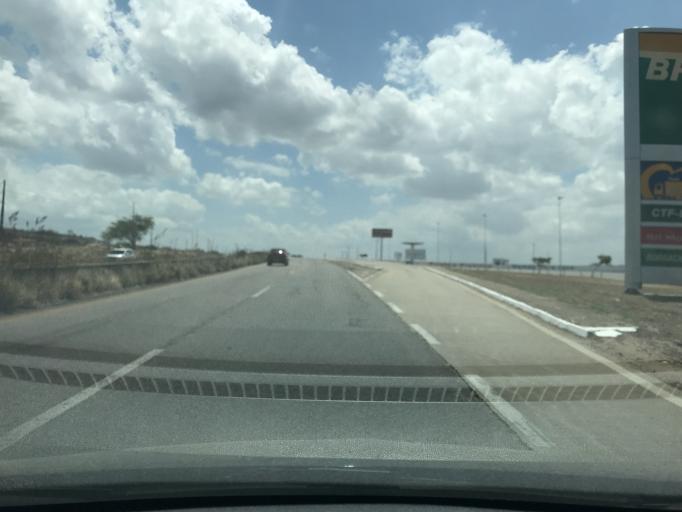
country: BR
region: Pernambuco
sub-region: Caruaru
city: Caruaru
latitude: -8.2942
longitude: -35.8832
